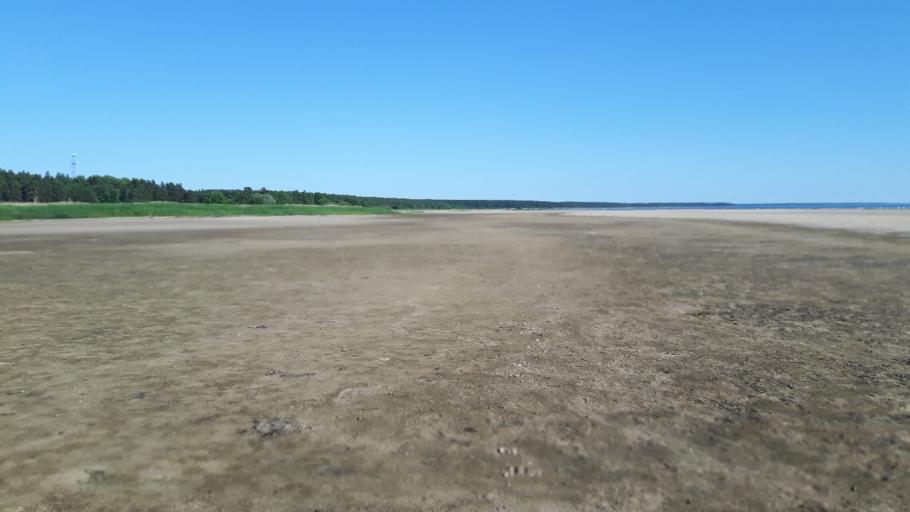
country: LV
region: Salacgrivas
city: Salacgriva
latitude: 57.6995
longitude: 24.3424
